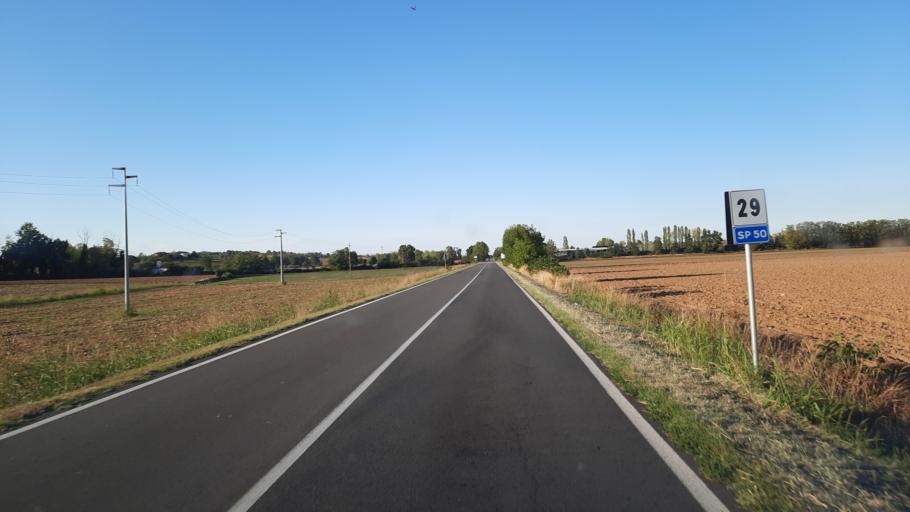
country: IT
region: Piedmont
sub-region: Provincia di Alessandria
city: Terruggia
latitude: 45.0711
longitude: 8.4680
